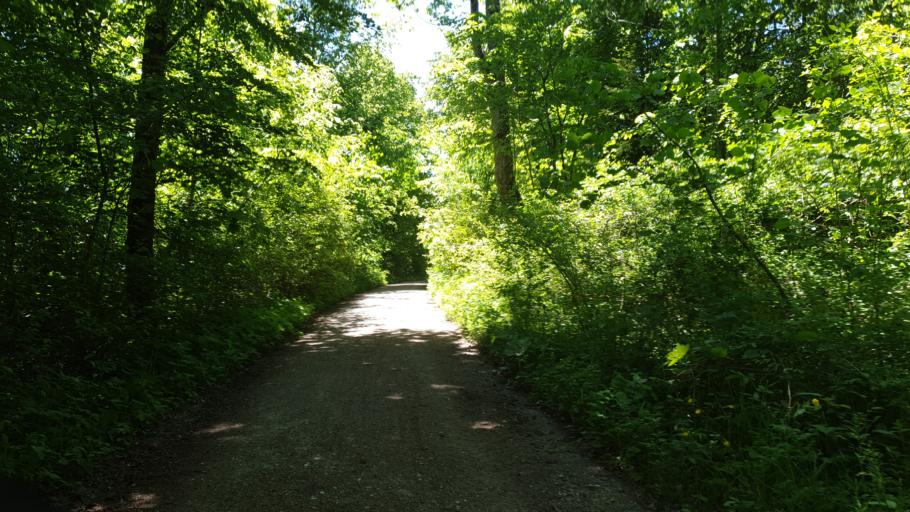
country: DE
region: Bavaria
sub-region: Upper Bavaria
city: Seeshaupt
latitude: 47.7916
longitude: 11.2889
